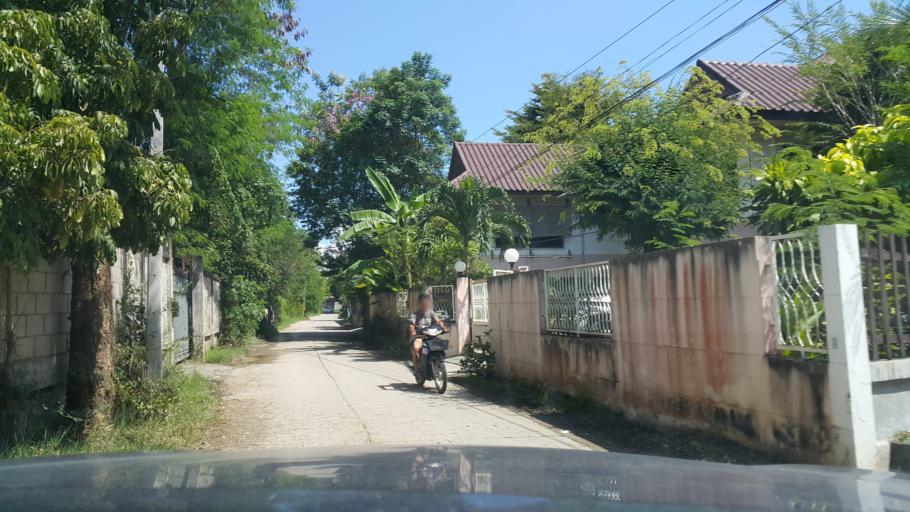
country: TH
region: Chiang Mai
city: Chiang Mai
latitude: 18.8462
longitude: 98.9817
